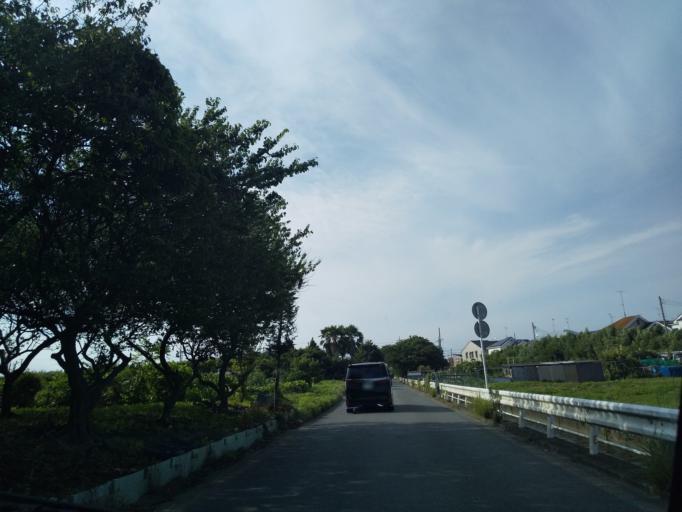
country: JP
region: Kanagawa
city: Zama
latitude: 35.4760
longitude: 139.3820
